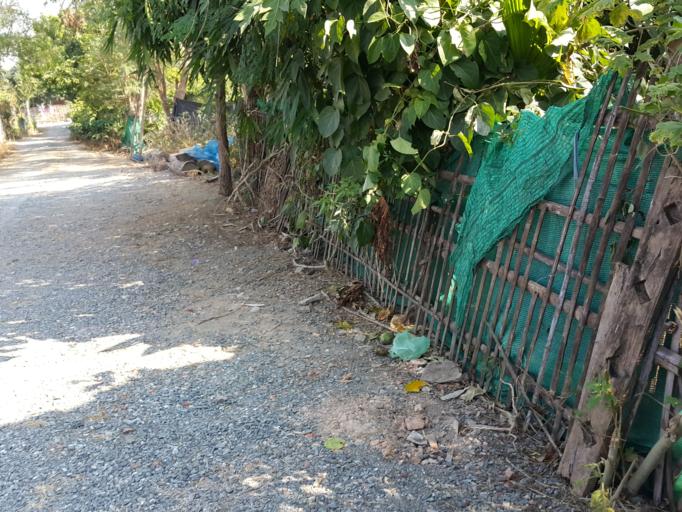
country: TH
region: Chiang Mai
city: San Kamphaeng
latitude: 18.6938
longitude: 99.1154
